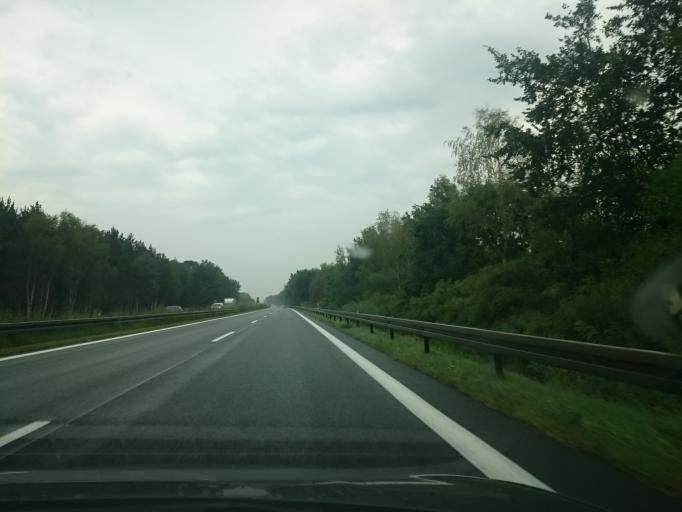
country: DE
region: Brandenburg
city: Brieselang
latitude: 52.6363
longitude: 12.9887
